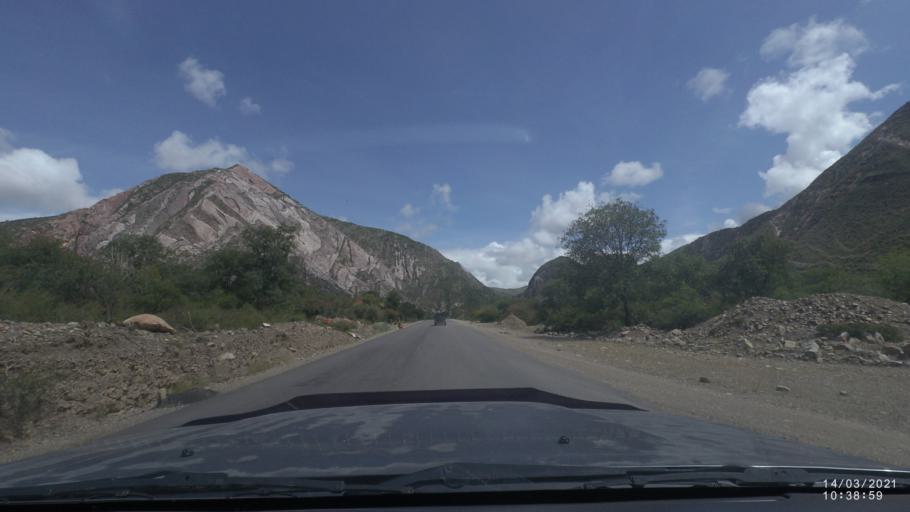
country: BO
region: Cochabamba
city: Cliza
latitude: -17.8901
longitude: -65.8946
